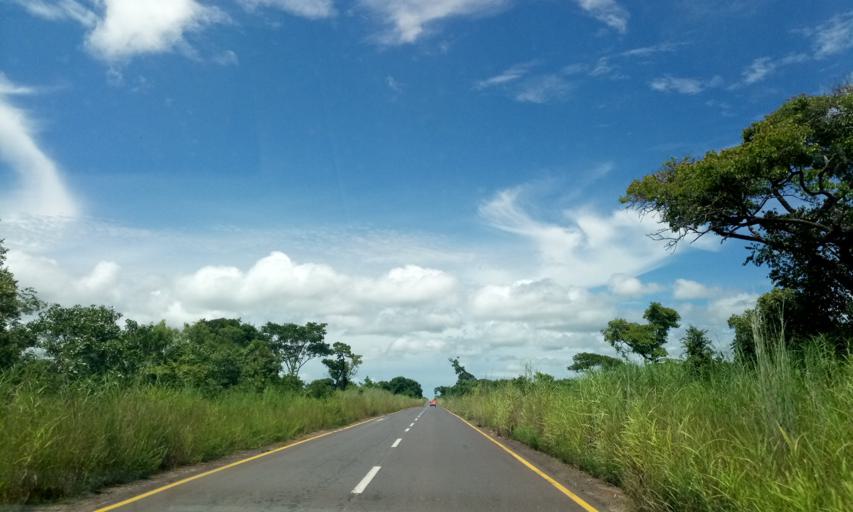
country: CD
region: Katanga
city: Lubumbashi
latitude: -11.1097
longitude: 27.9705
